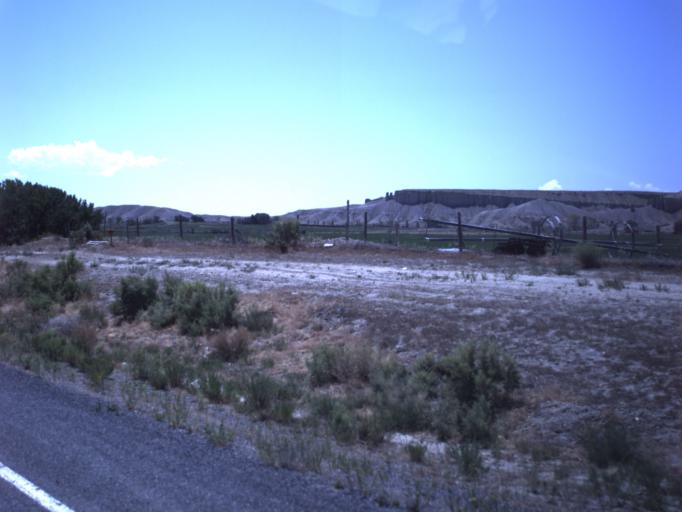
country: US
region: Utah
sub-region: Emery County
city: Orangeville
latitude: 39.2261
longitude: -111.0721
